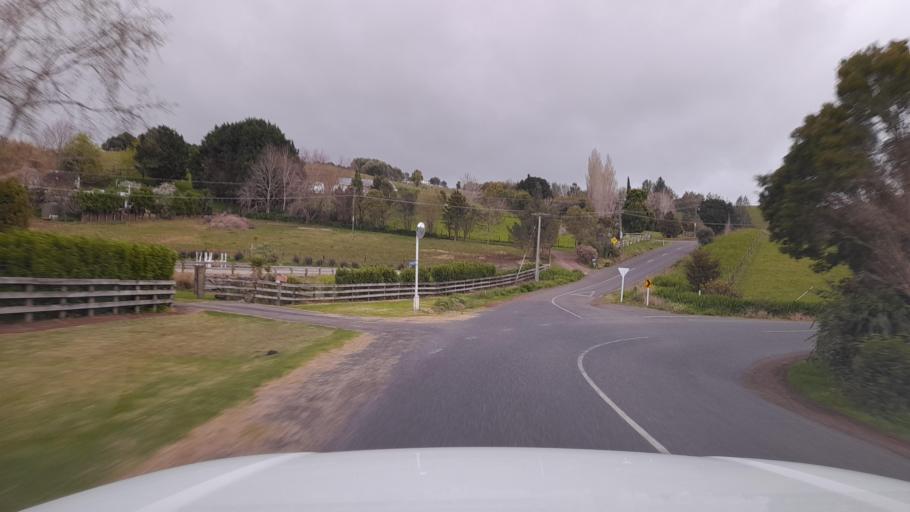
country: NZ
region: Northland
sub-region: Whangarei
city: Maungatapere
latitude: -35.6522
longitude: 174.2192
